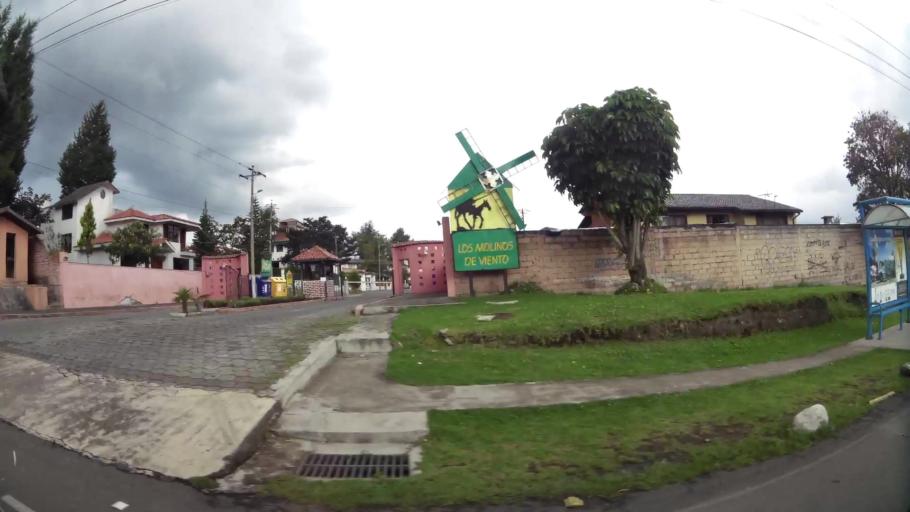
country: EC
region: Pichincha
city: Sangolqui
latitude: -0.3415
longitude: -78.4496
